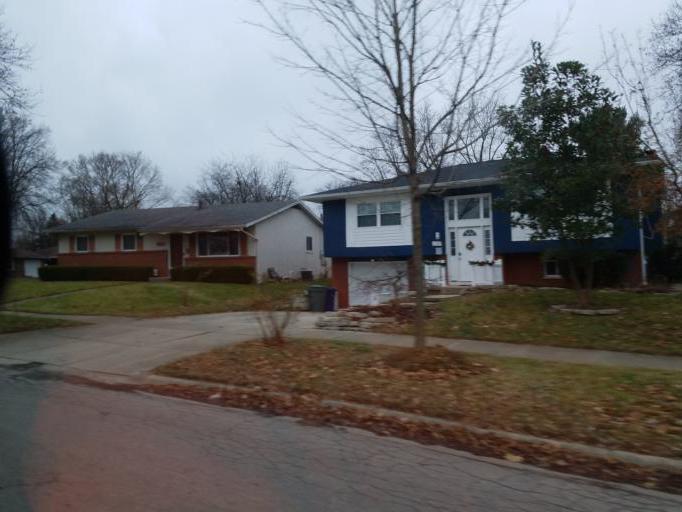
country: US
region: Ohio
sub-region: Franklin County
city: Worthington
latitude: 40.0946
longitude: -82.9838
